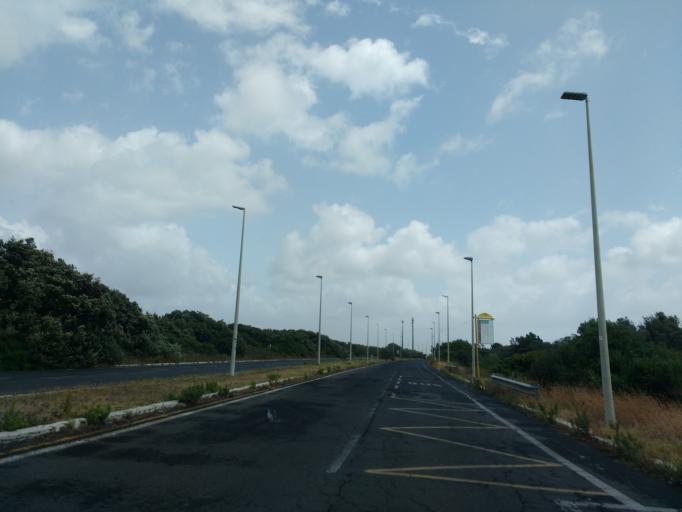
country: IT
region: Latium
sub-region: Citta metropolitana di Roma Capitale
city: Acilia-Castel Fusano-Ostia Antica
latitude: 41.7048
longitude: 12.3436
